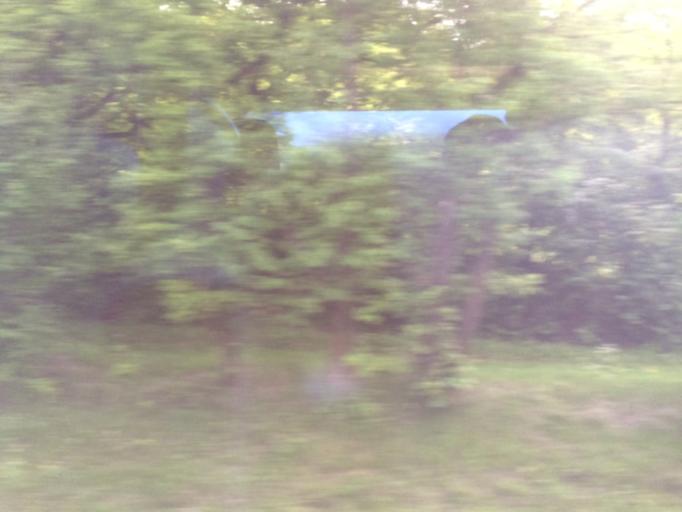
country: DE
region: Bavaria
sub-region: Regierungsbezirk Unterfranken
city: Rottendorf
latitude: 49.7841
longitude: 10.0169
